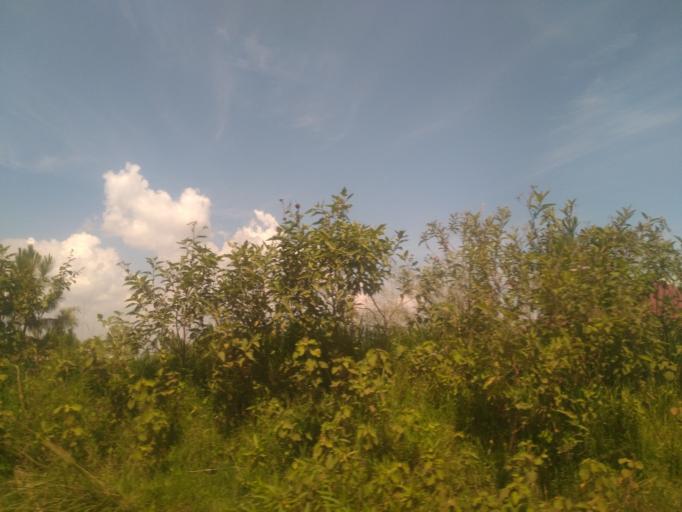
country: UG
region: Central Region
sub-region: Wakiso District
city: Entebbe
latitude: 0.0378
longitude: 32.4287
